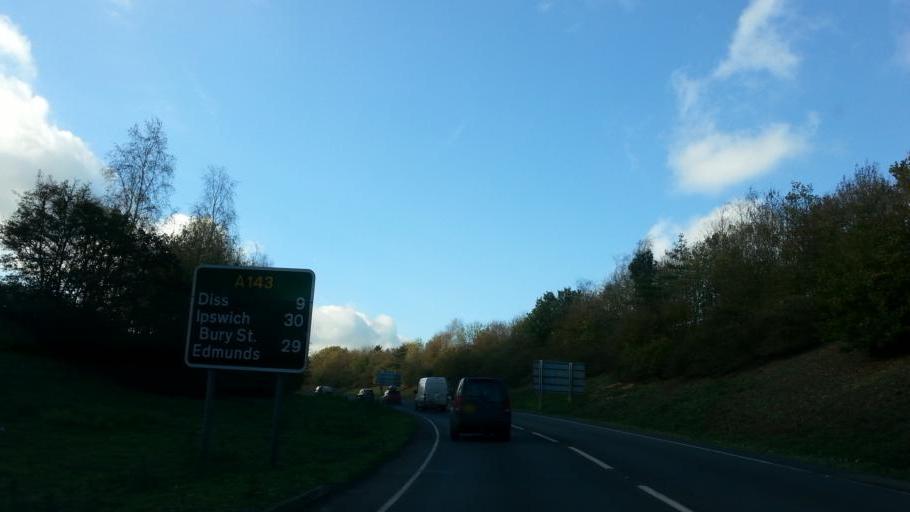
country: GB
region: England
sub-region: Norfolk
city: Harleston
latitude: 52.3931
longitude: 1.2827
